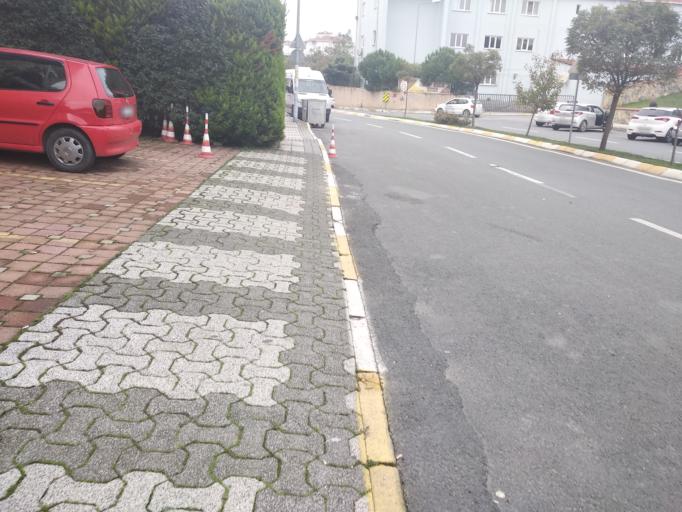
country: TR
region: Istanbul
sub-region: Atasehir
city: Atasehir
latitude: 40.9834
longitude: 29.1233
